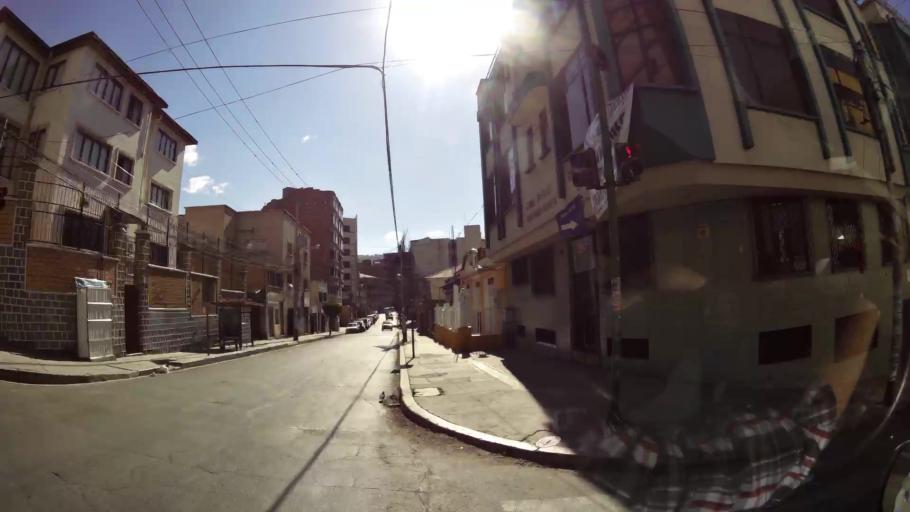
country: BO
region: La Paz
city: La Paz
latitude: -16.5054
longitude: -68.1335
